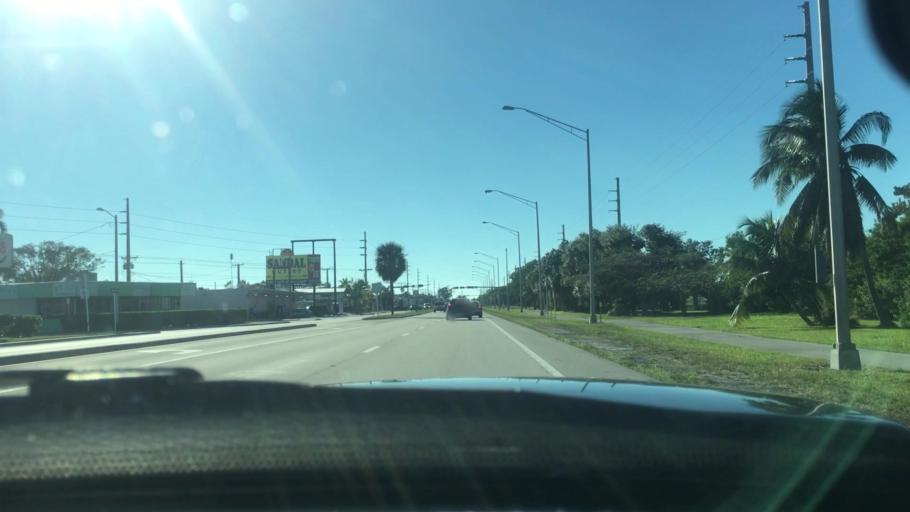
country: US
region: Florida
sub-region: Monroe County
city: Stock Island
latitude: 24.5737
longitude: -81.7405
